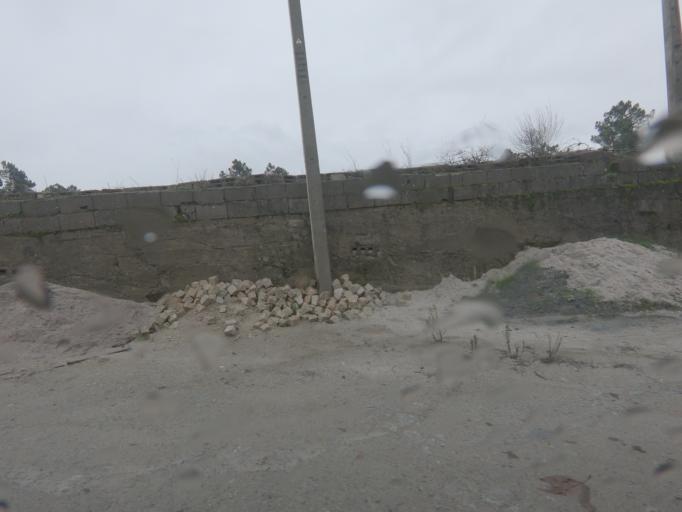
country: PT
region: Vila Real
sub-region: Peso da Regua
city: Peso da Regua
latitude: 41.1840
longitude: -7.7148
